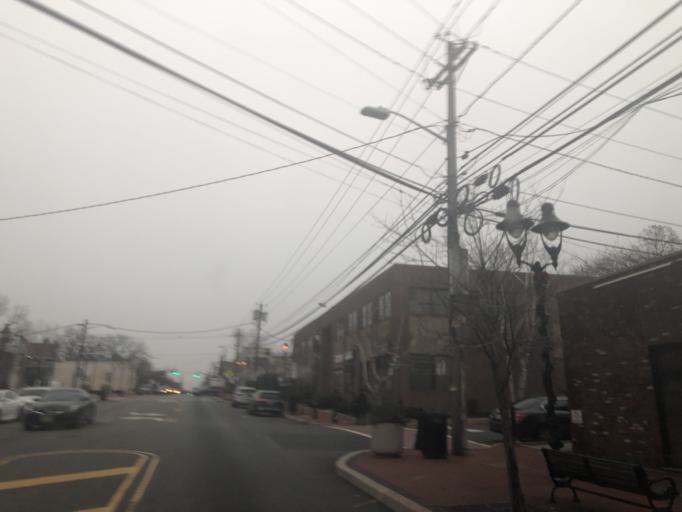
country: US
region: New Jersey
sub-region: Essex County
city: Maplewood
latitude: 40.7199
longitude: -74.2745
